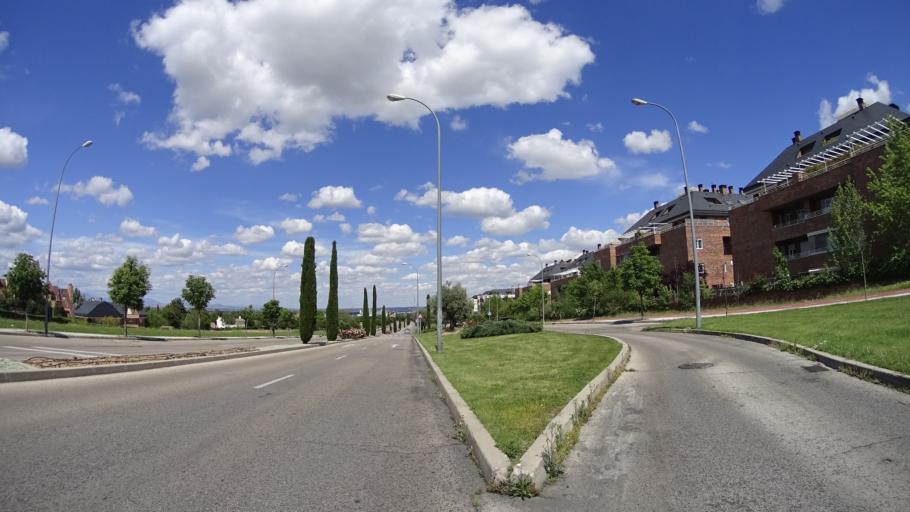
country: ES
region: Madrid
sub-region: Provincia de Madrid
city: Majadahonda
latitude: 40.4615
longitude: -3.8652
